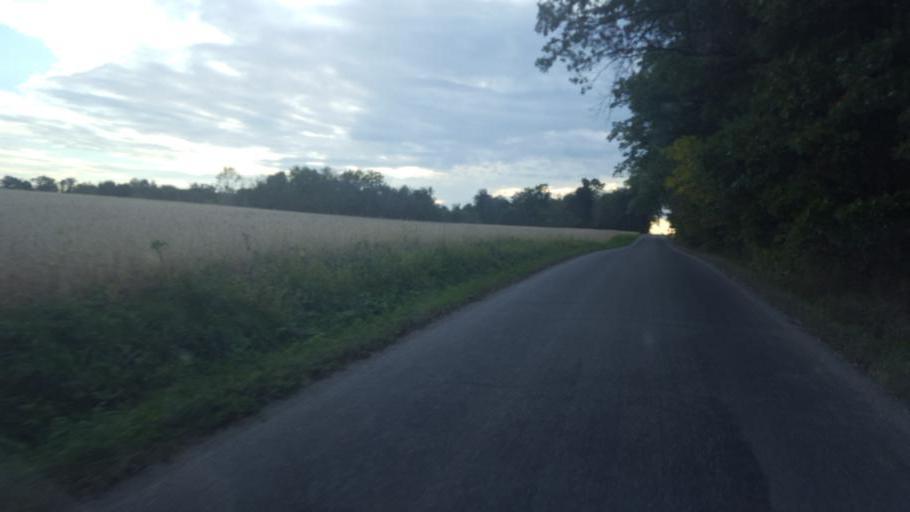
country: US
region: Ohio
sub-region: Ashland County
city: Loudonville
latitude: 40.7111
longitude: -82.2169
